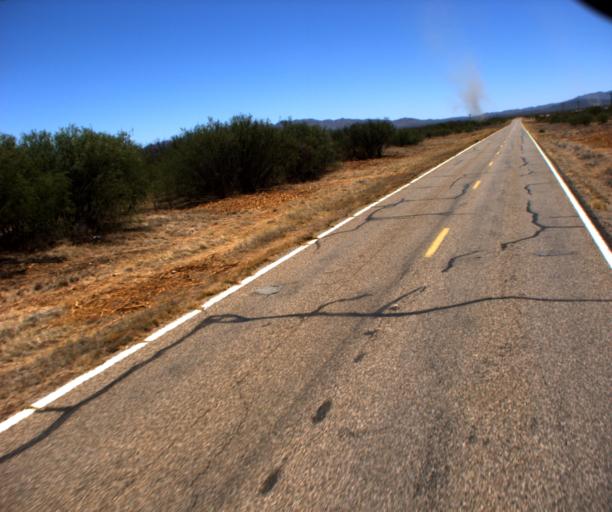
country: US
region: Arizona
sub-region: Pima County
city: Ajo
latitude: 32.1861
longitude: -112.3773
